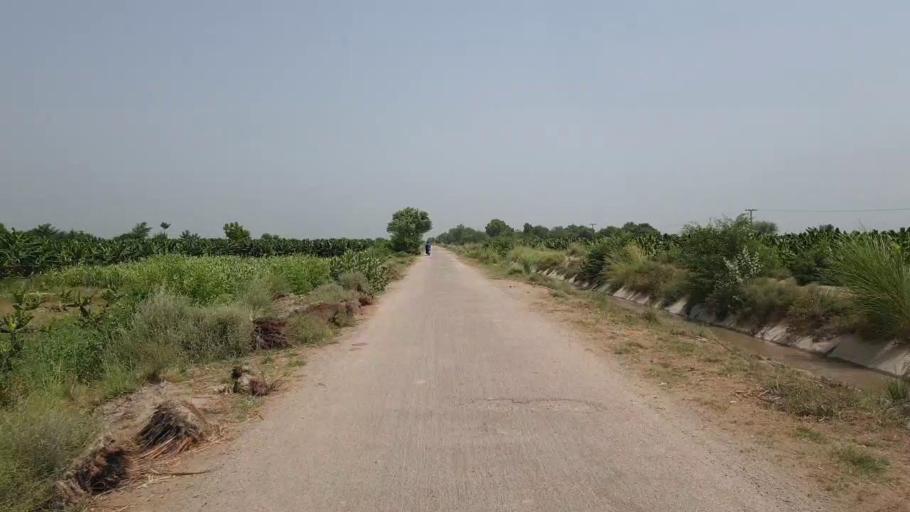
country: PK
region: Sindh
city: Nawabshah
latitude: 26.2836
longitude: 68.3110
